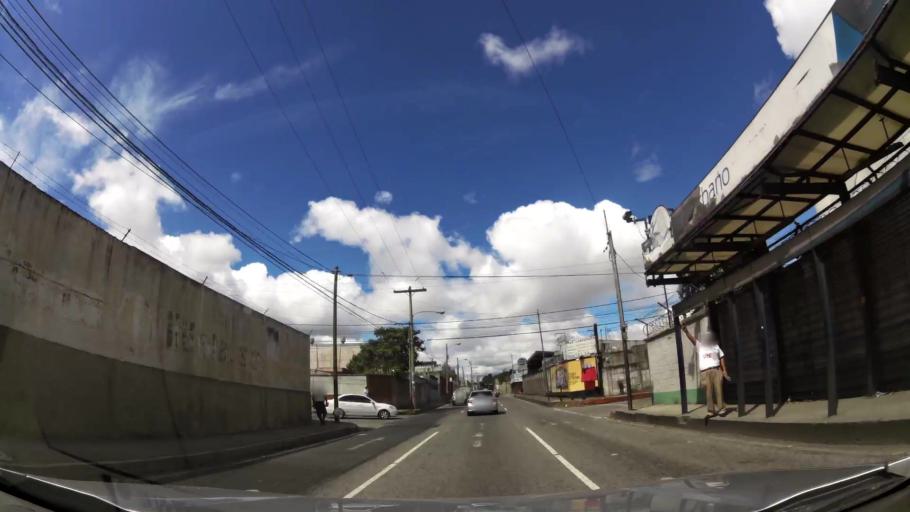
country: GT
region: Guatemala
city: Guatemala City
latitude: 14.6034
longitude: -90.5307
